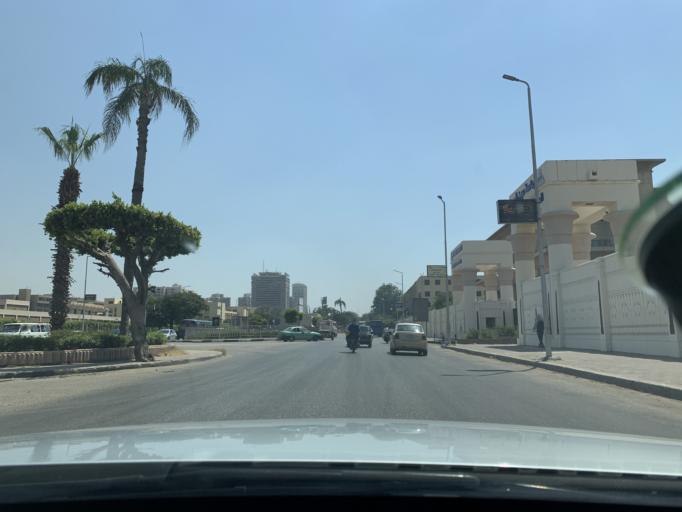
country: EG
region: Muhafazat al Qahirah
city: Cairo
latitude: 30.0781
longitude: 31.2894
